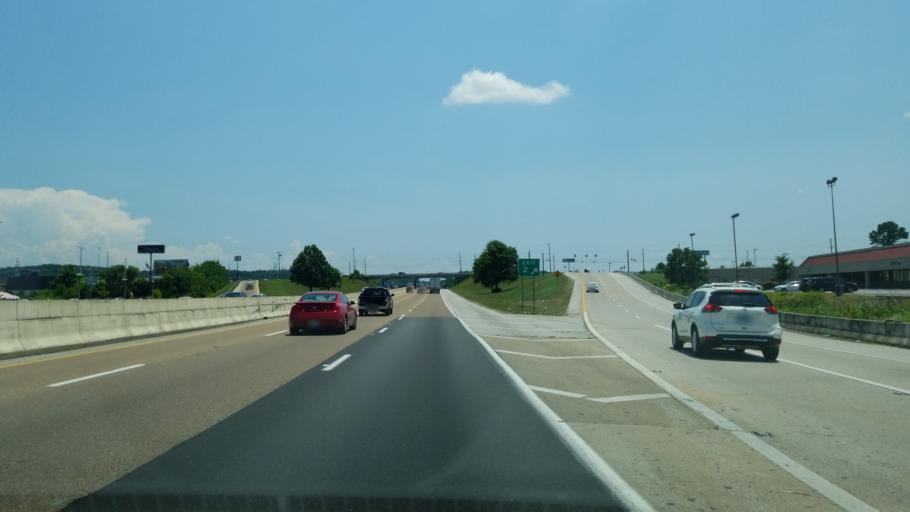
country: US
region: Tennessee
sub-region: Hamilton County
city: East Chattanooga
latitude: 35.0572
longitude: -85.1921
